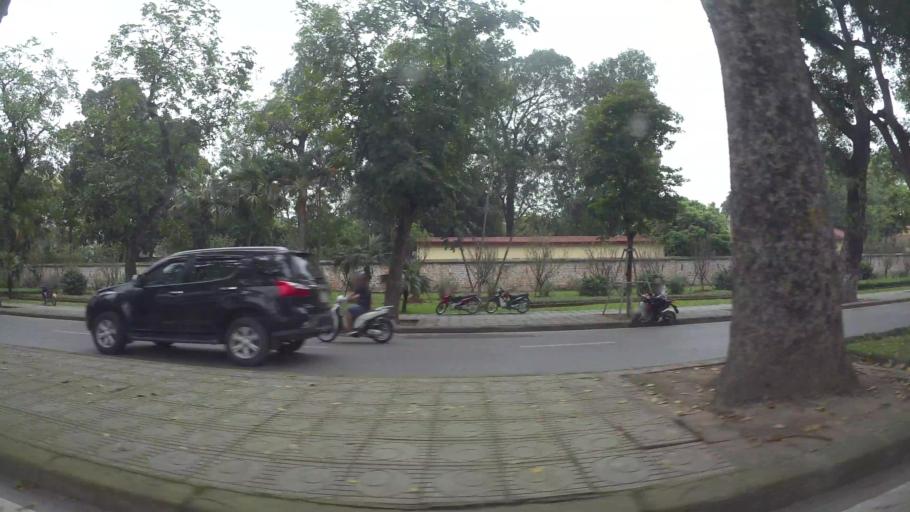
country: VN
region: Ha Noi
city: Hanoi
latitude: 21.0376
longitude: 105.8395
